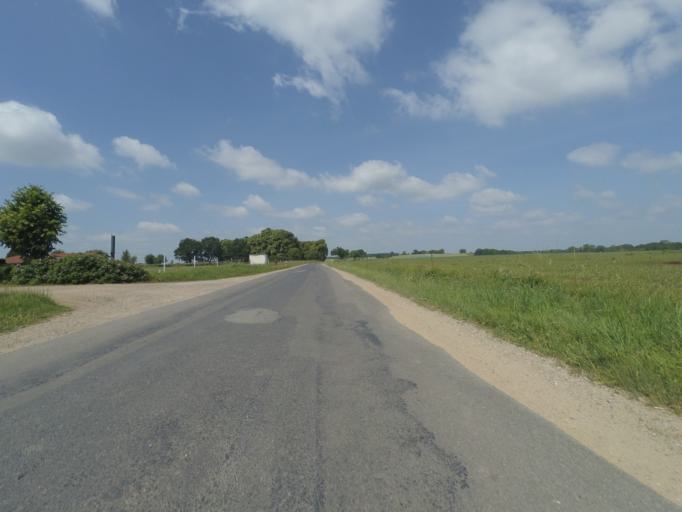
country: DE
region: Mecklenburg-Vorpommern
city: Lubz
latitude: 53.4068
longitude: 12.0138
